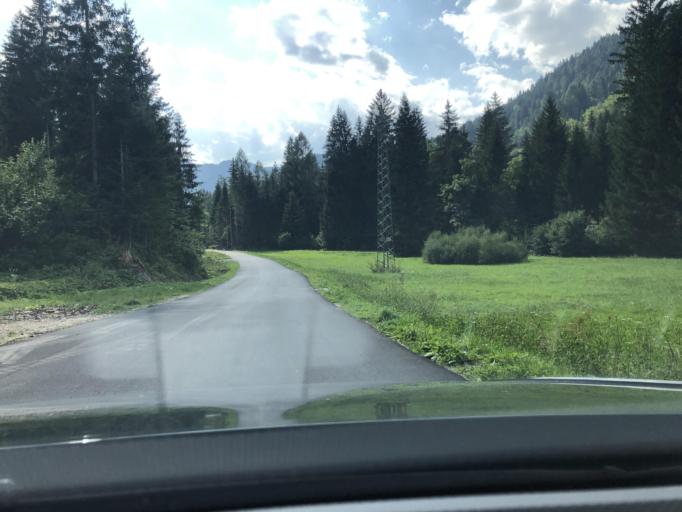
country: IT
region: Veneto
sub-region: Provincia di Belluno
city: Santo Stefano di Cadore
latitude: 46.5602
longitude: 12.5672
